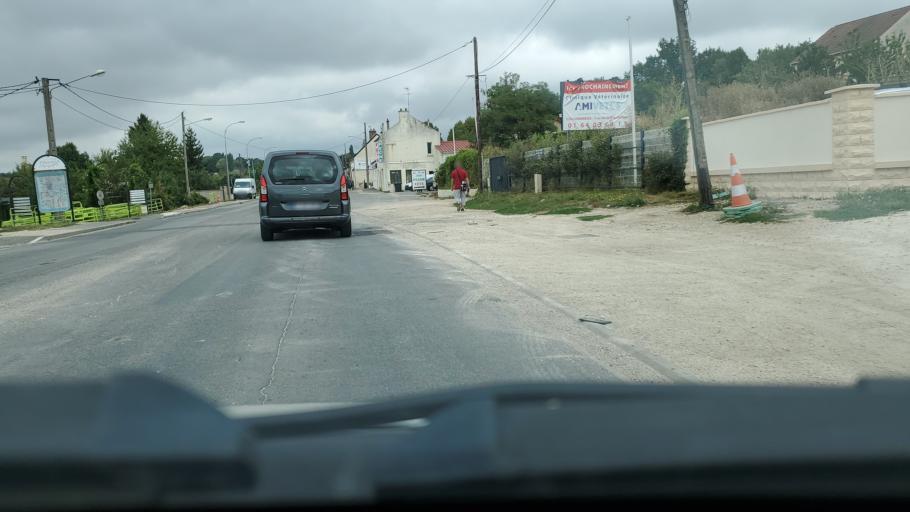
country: FR
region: Ile-de-France
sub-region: Departement de Seine-et-Marne
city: Mouroux
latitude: 48.8211
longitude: 3.0469
